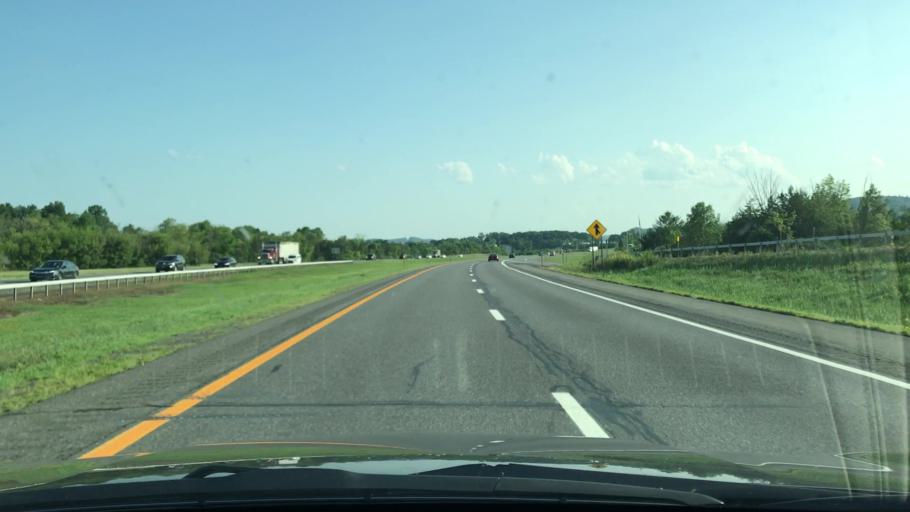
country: US
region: New York
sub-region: Greene County
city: Coxsackie
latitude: 42.3927
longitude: -73.8253
